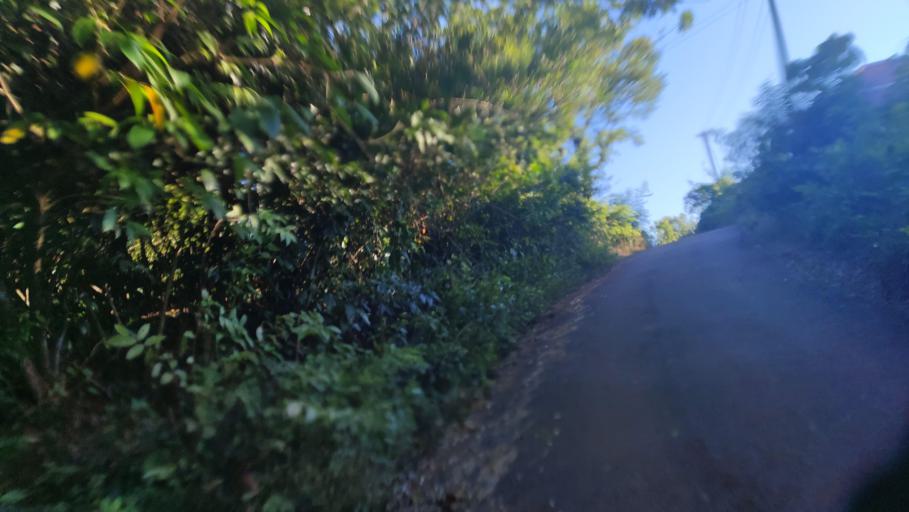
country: IN
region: Kerala
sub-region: Kasaragod District
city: Kasaragod
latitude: 12.5021
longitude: 75.0792
